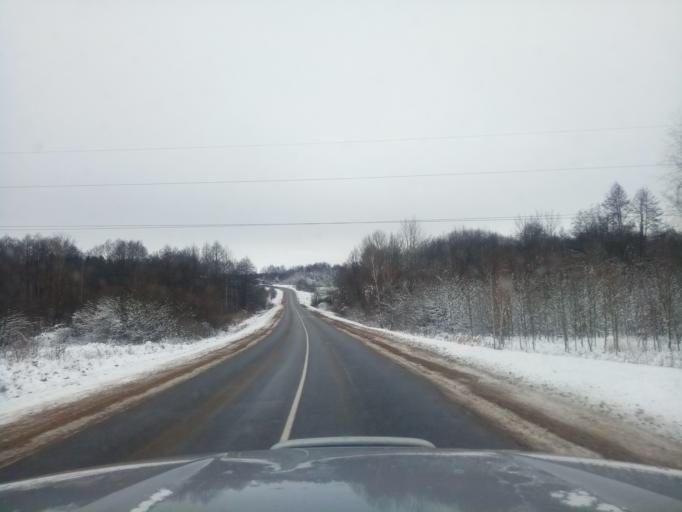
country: BY
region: Minsk
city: Kapyl'
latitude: 53.1513
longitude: 27.1217
